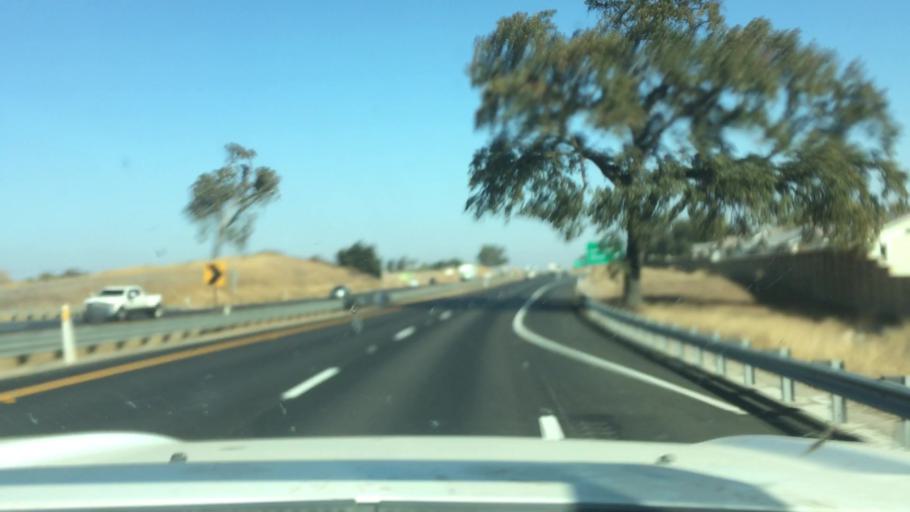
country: US
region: California
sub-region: San Luis Obispo County
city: Templeton
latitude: 35.5851
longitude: -120.6986
